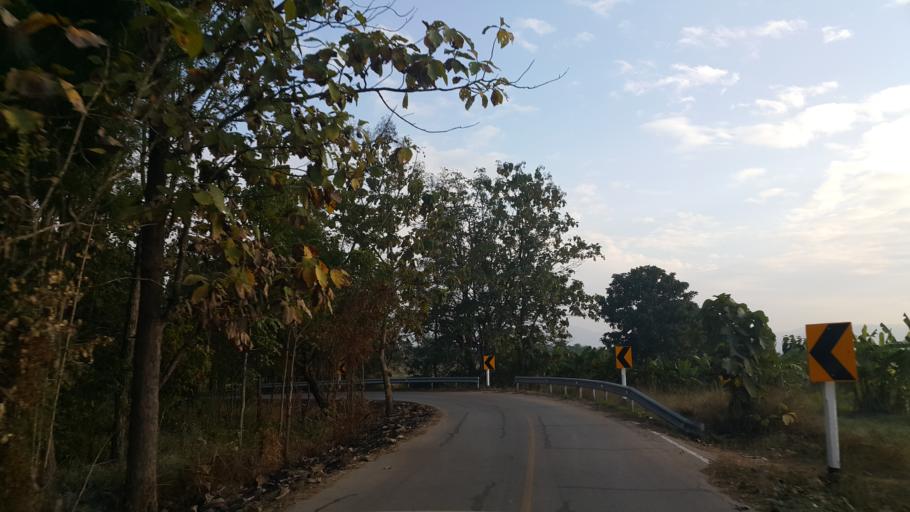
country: TH
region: Lampang
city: Sop Prap
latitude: 17.9155
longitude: 99.3293
